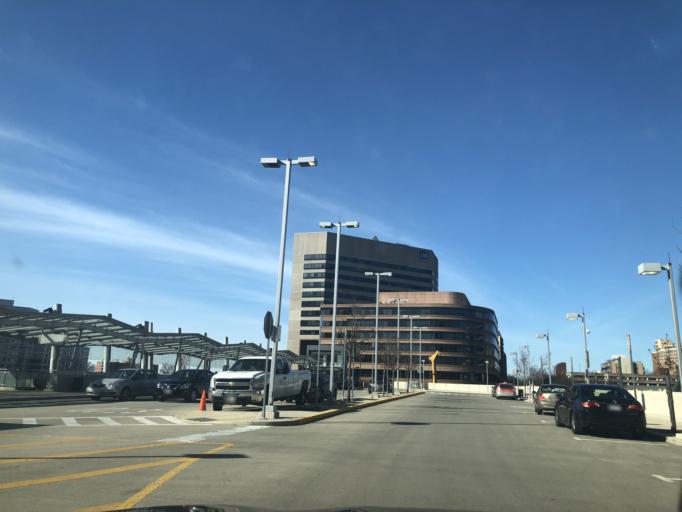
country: US
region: Maryland
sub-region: Montgomery County
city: Silver Spring
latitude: 38.9935
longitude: -77.0295
